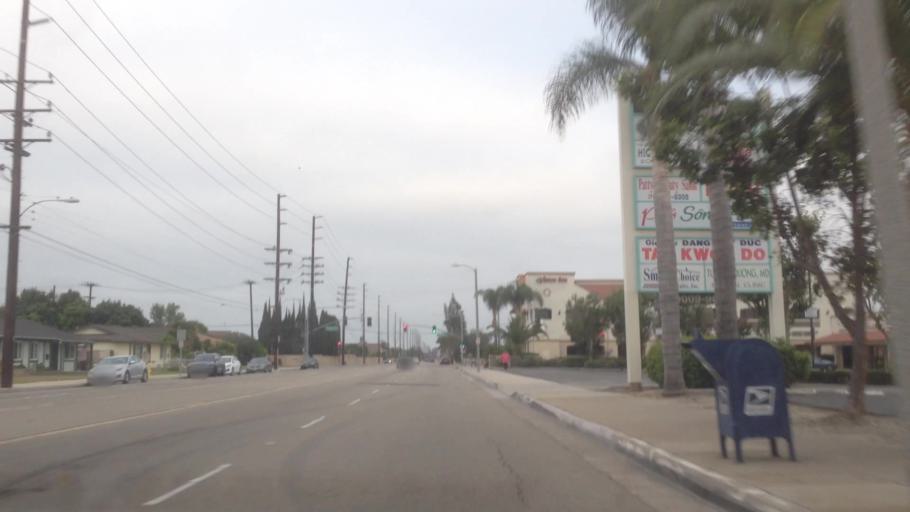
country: US
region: California
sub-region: Orange County
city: Midway City
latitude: 33.7376
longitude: -117.9705
